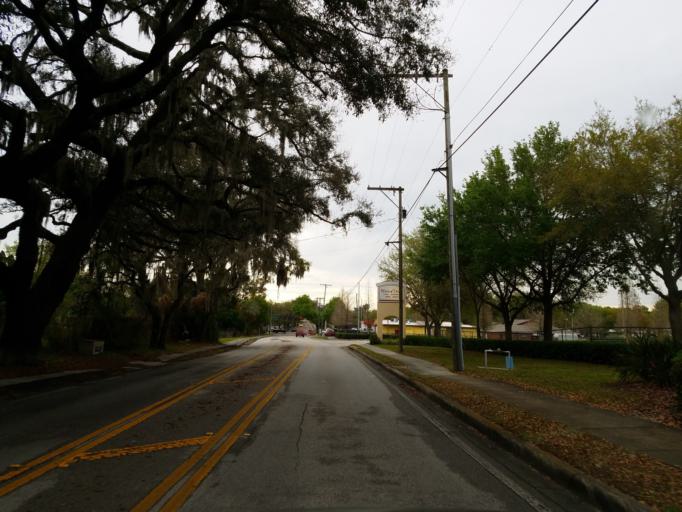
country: US
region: Florida
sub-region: Hillsborough County
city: Valrico
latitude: 27.9359
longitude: -82.2445
